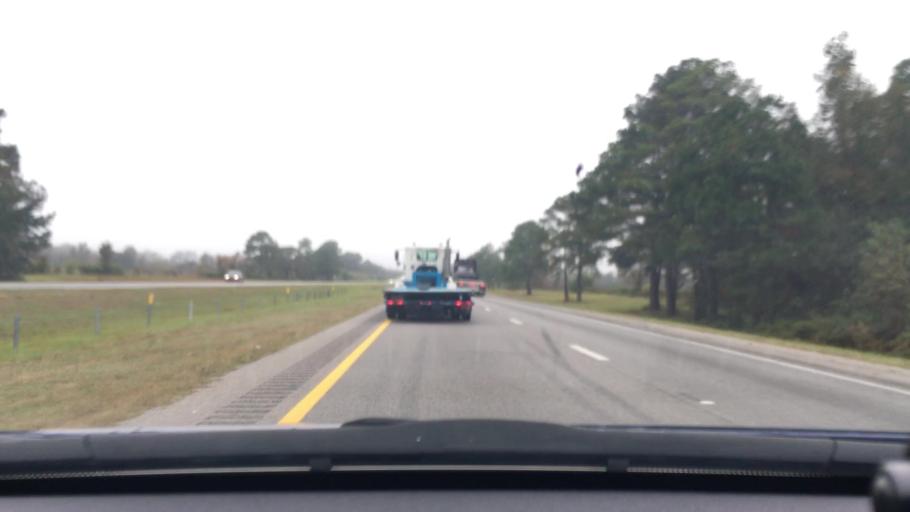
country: US
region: South Carolina
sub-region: Lee County
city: Bishopville
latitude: 34.1892
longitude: -80.2433
